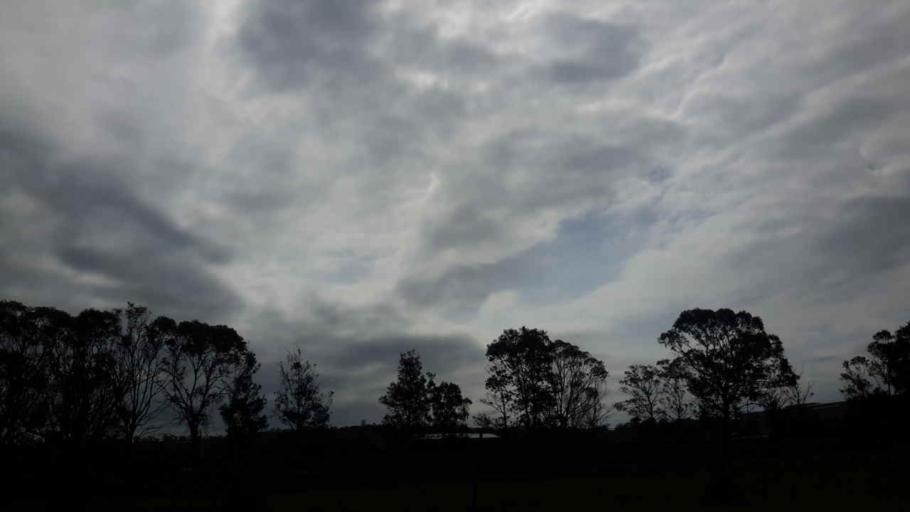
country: AU
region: New South Wales
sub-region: Campbelltown Municipality
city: Glen Alpine
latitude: -34.1136
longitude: 150.7435
